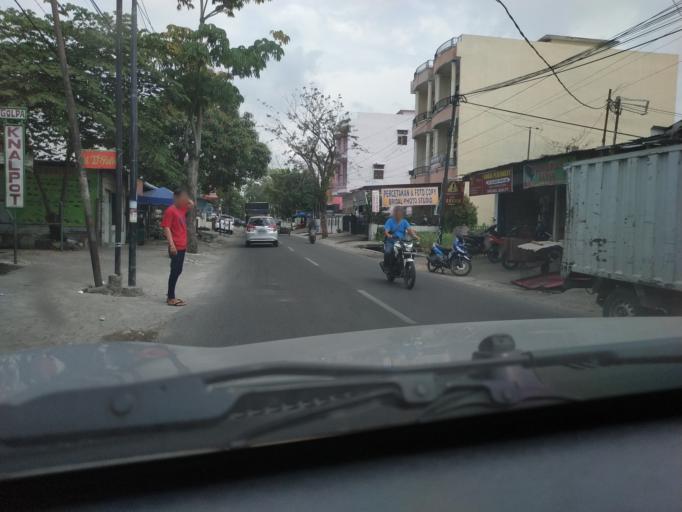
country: ID
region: North Sumatra
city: Sunggal
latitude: 3.5844
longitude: 98.6378
